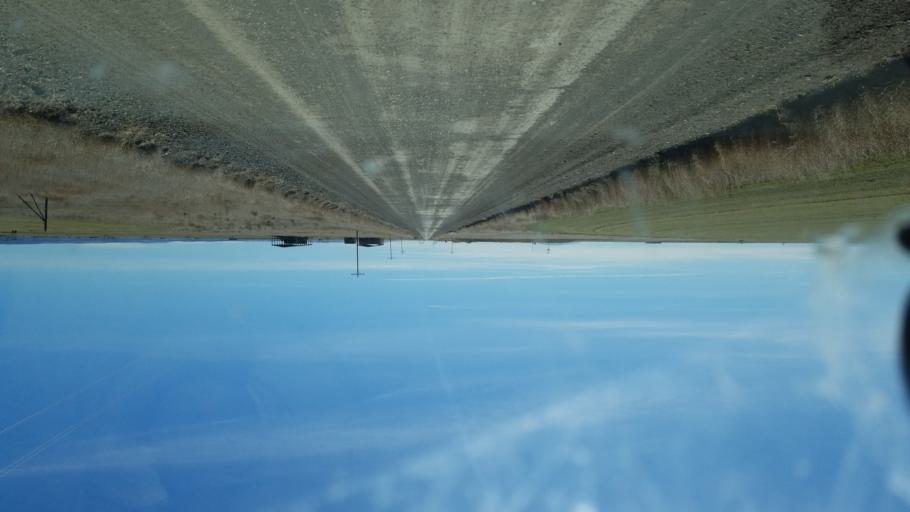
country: US
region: Colorado
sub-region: Rio Grande County
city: Monte Vista
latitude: 37.4122
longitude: -106.1303
